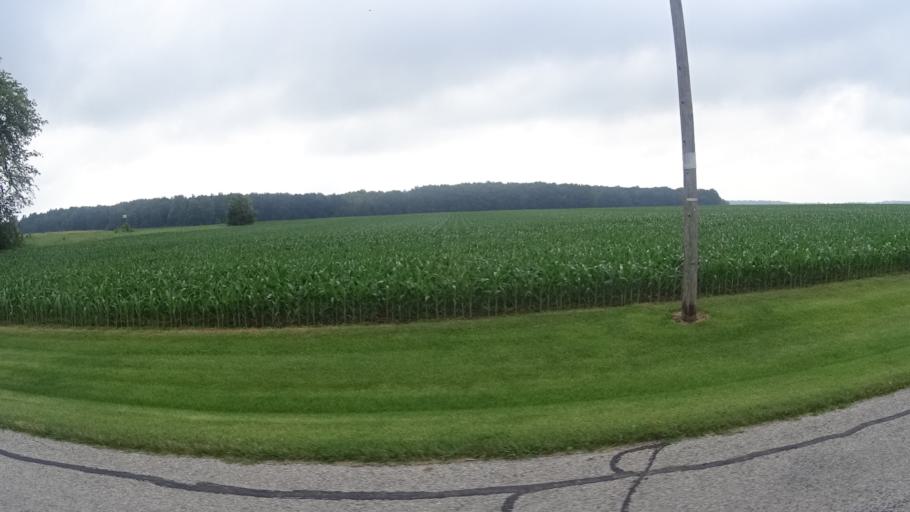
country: US
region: Ohio
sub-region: Erie County
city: Milan
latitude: 41.2894
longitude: -82.5118
